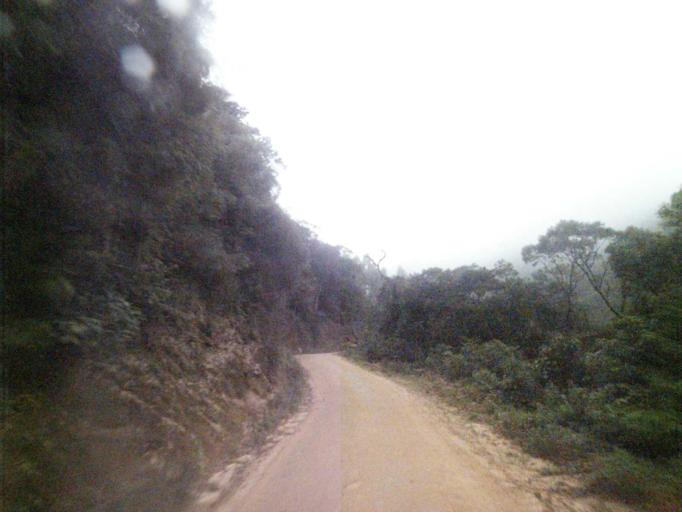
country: BR
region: Santa Catarina
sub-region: Anitapolis
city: Anitapolis
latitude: -27.8220
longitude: -49.1365
